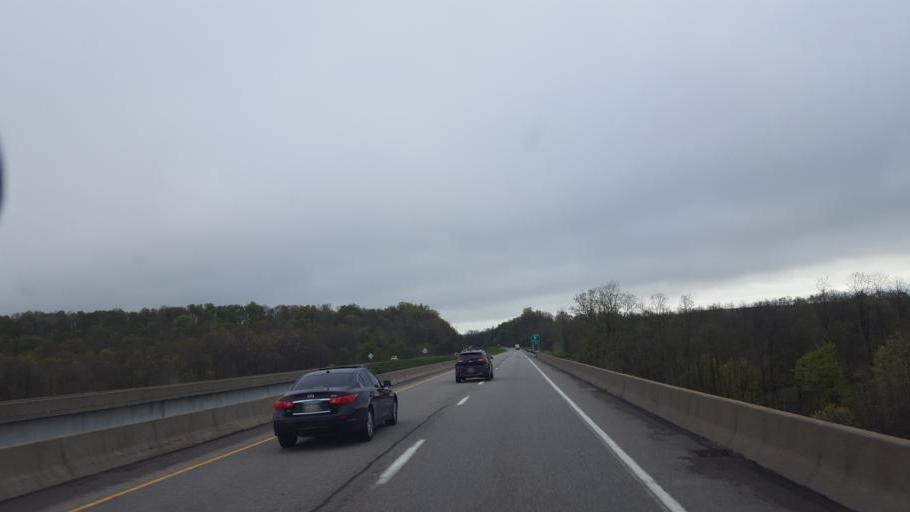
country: US
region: Pennsylvania
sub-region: Mercer County
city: Mercer
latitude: 41.2302
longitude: -80.1619
